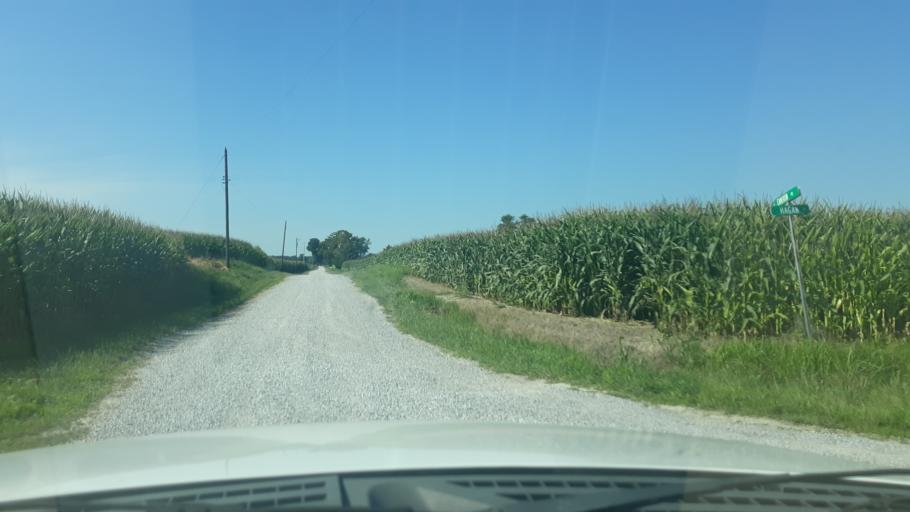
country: US
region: Illinois
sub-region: Saline County
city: Eldorado
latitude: 37.8558
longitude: -88.4849
